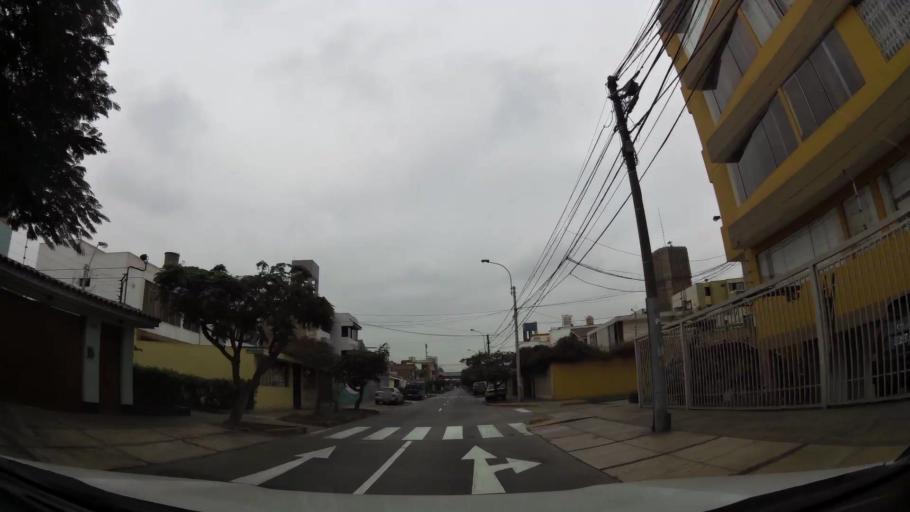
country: PE
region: Lima
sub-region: Lima
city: San Luis
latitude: -12.1052
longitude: -77.0033
